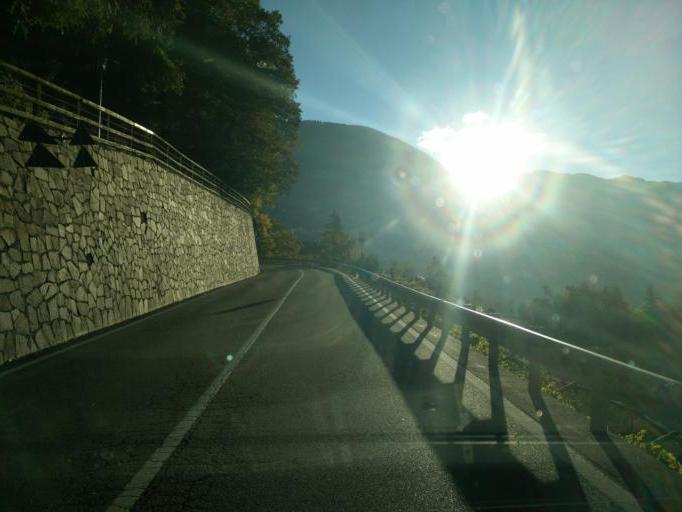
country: IT
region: Trentino-Alto Adige
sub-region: Bolzano
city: Caines
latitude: 46.6953
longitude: 11.1699
